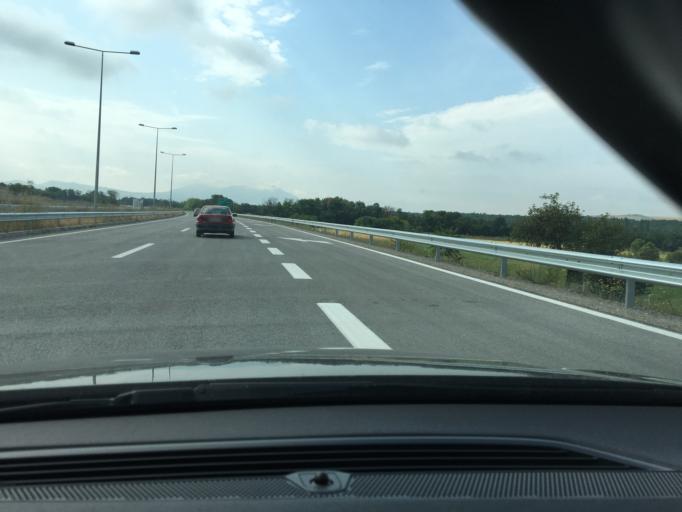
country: MK
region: Sveti Nikole
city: Sveti Nikole
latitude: 41.8539
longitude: 21.9635
